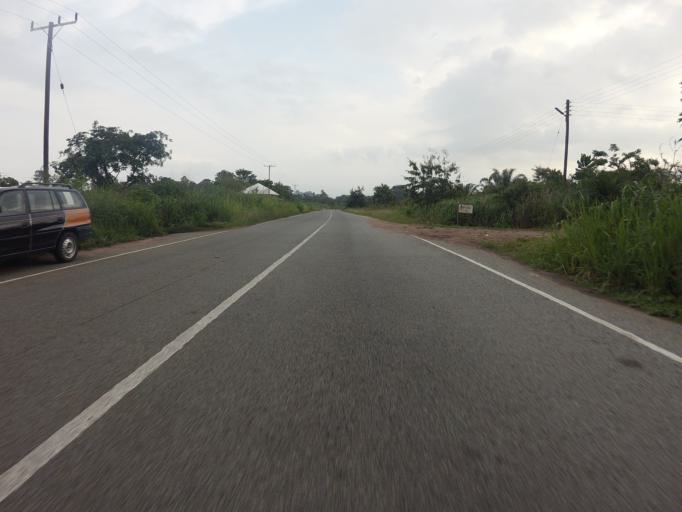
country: GH
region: Volta
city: Ho
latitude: 6.7856
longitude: 0.4510
